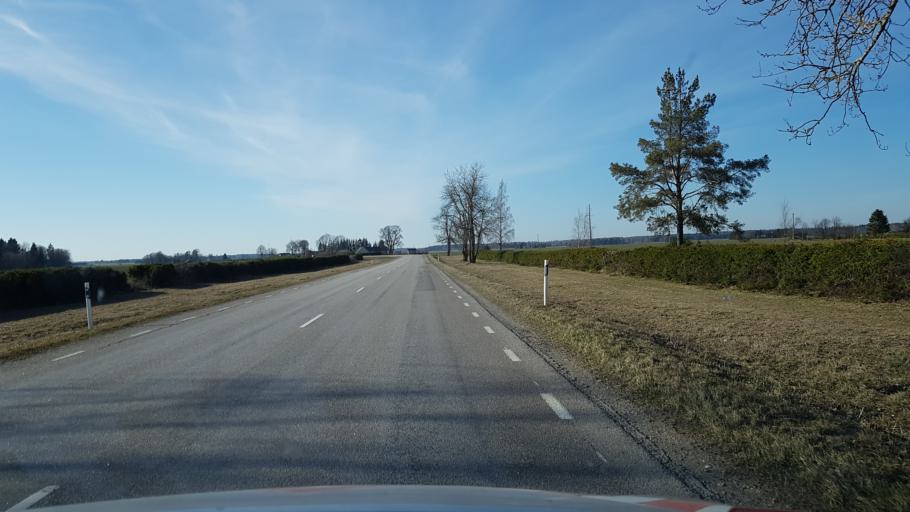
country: EE
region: Laeaene-Virumaa
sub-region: Vinni vald
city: Vinni
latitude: 59.2250
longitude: 26.5273
